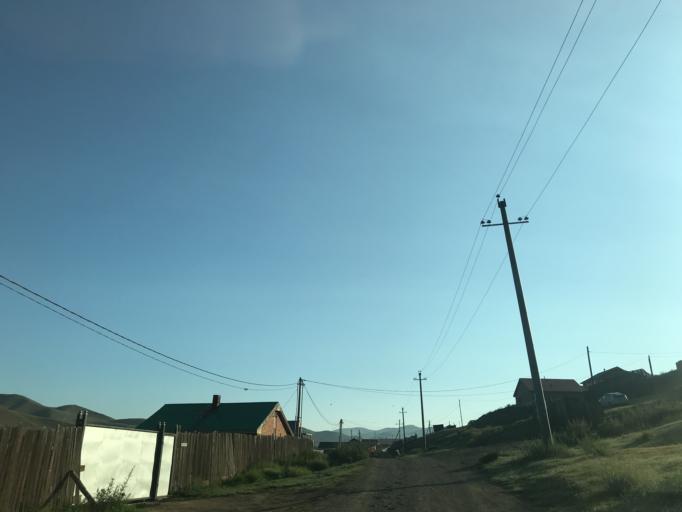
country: MN
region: Ulaanbaatar
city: Ulaanbaatar
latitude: 47.9884
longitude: 106.9634
